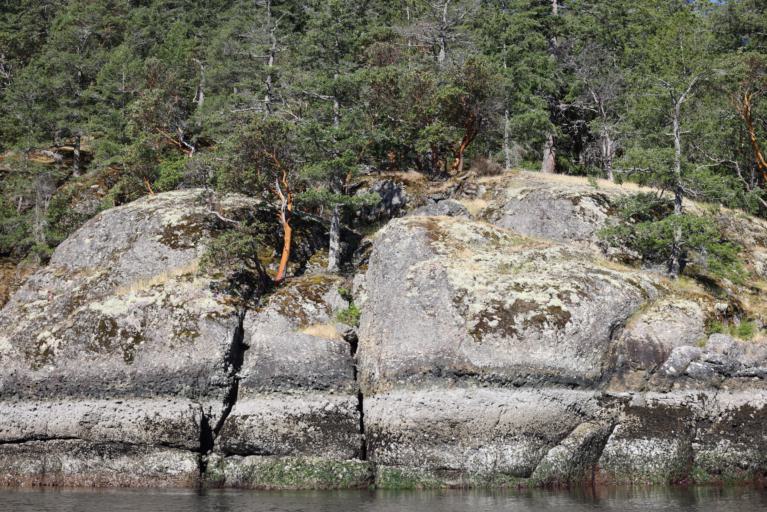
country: CA
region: British Columbia
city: North Cowichan
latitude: 48.7977
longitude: -123.5617
